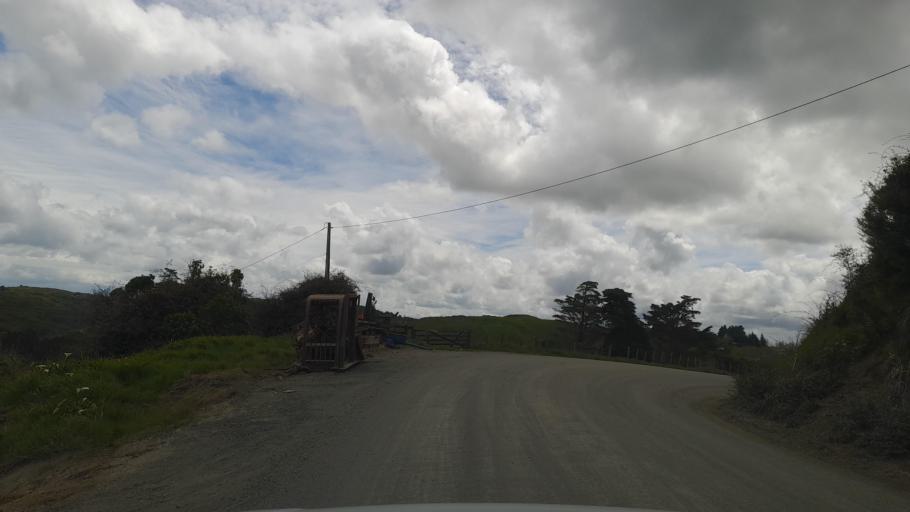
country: NZ
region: Auckland
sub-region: Auckland
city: Wellsford
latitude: -36.1527
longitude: 174.3530
